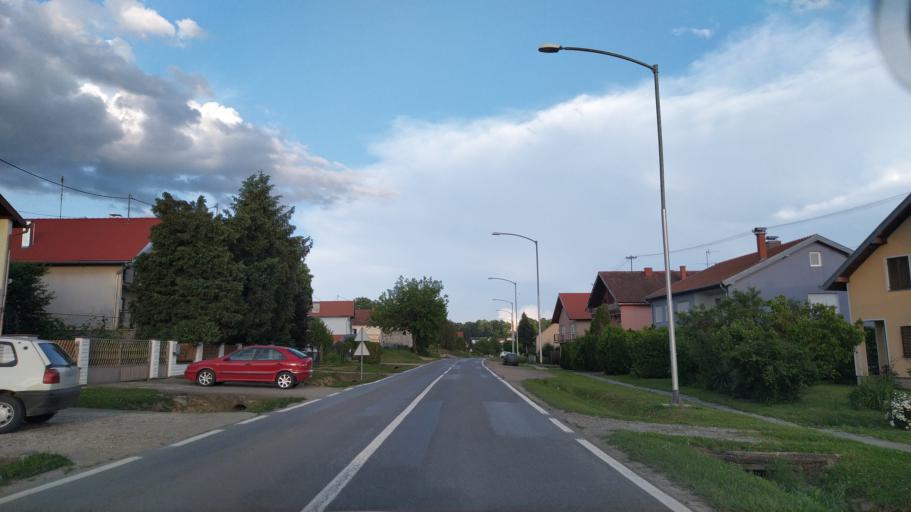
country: HR
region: Osjecko-Baranjska
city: Martin
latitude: 45.4912
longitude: 18.0680
